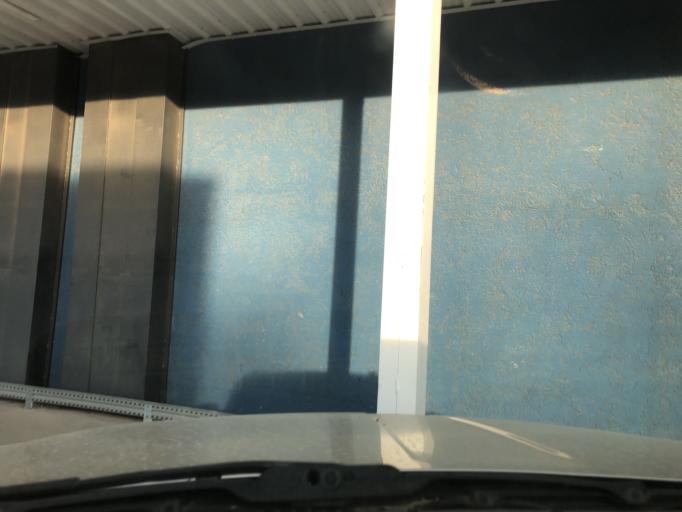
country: AR
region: Cordoba
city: Jesus Maria
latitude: -30.9763
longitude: -64.0831
